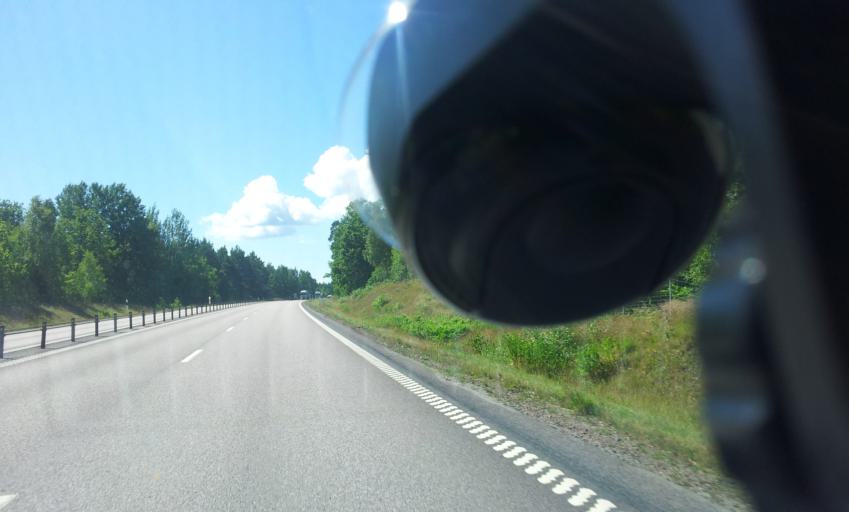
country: SE
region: Kalmar
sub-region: Oskarshamns Kommun
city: Paskallavik
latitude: 57.2067
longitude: 16.4369
